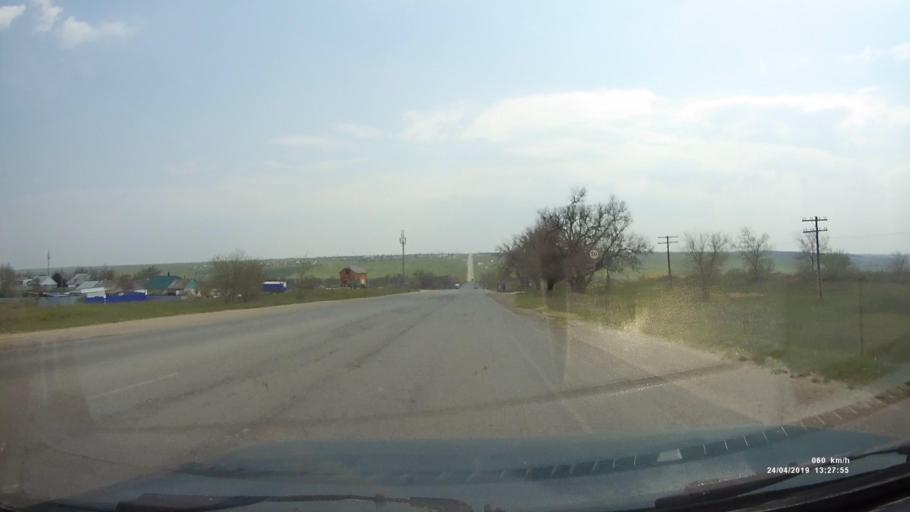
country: RU
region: Kalmykiya
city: Arshan'
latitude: 46.2770
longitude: 44.2283
